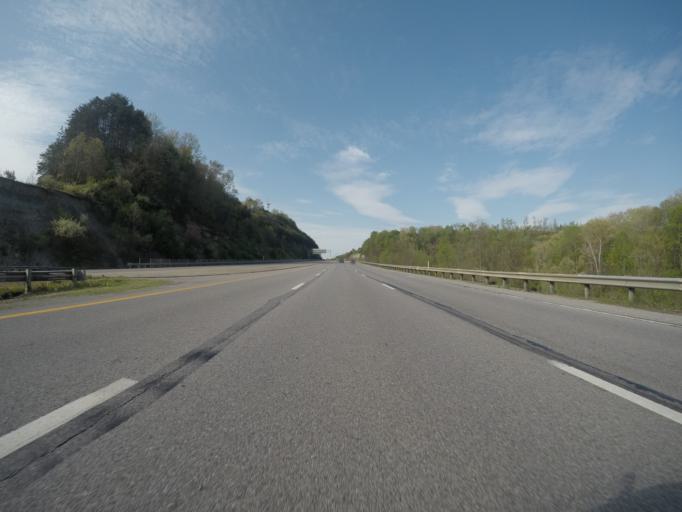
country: US
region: West Virginia
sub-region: Kanawha County
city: South Charleston
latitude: 38.3399
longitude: -81.7062
